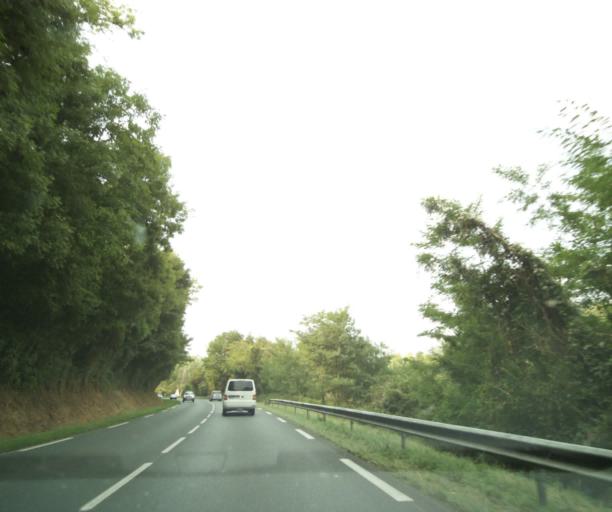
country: FR
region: Centre
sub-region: Departement de l'Indre
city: Clion
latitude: 46.9587
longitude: 1.2145
